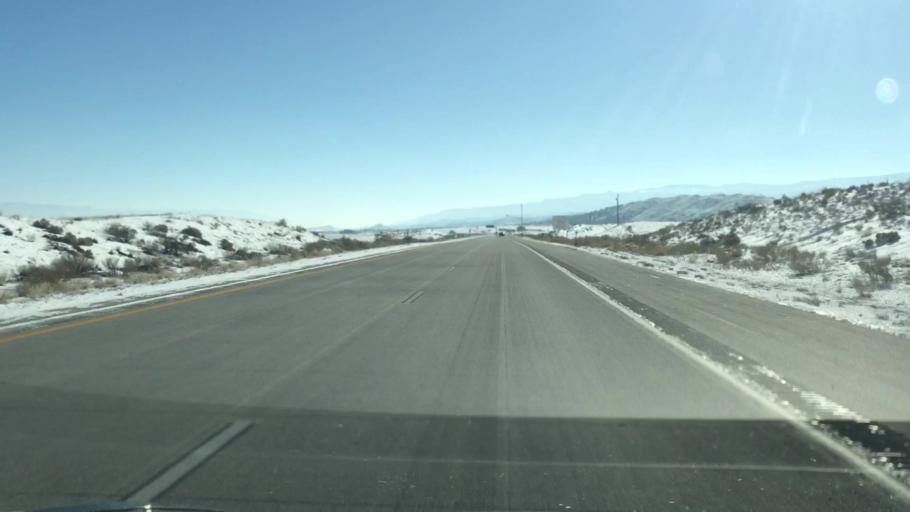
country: US
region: Colorado
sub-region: Mesa County
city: Loma
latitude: 39.1859
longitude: -108.8337
